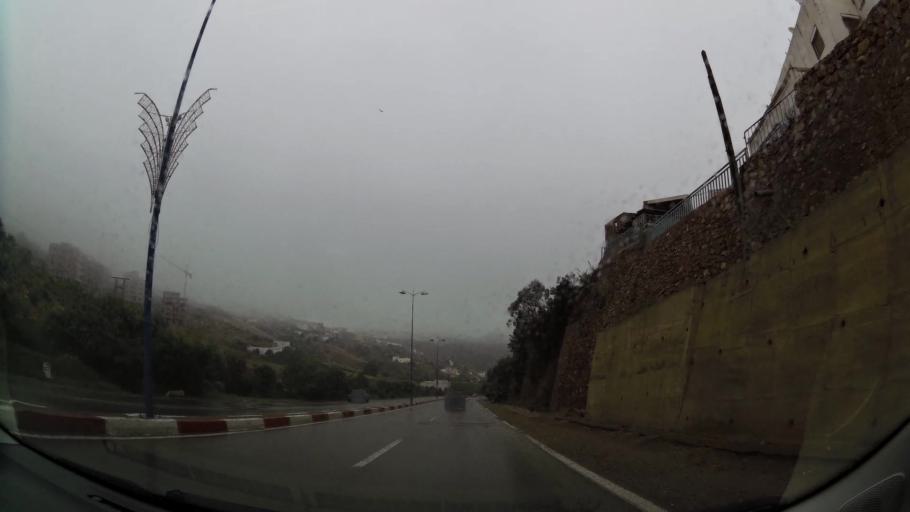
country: MA
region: Taza-Al Hoceima-Taounate
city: Al Hoceima
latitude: 35.2254
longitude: -3.9292
